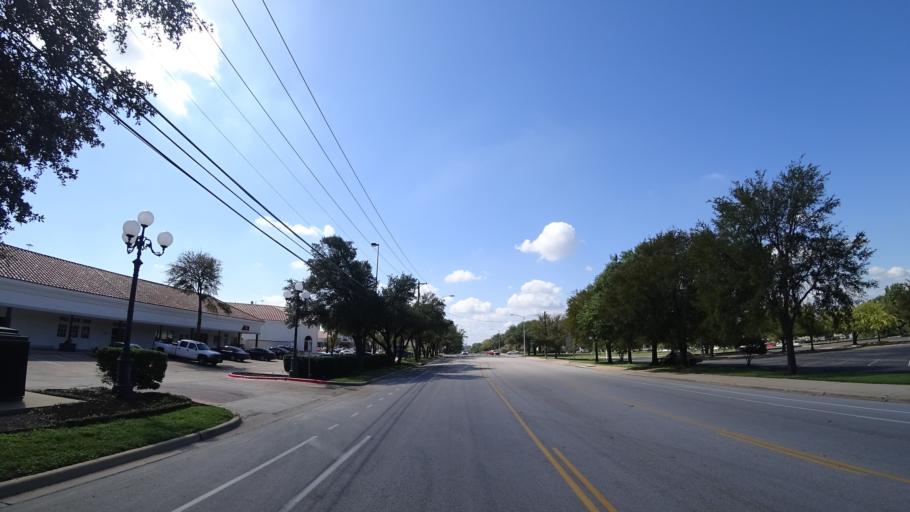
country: US
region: Texas
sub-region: Travis County
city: Austin
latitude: 30.3271
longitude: -97.7078
